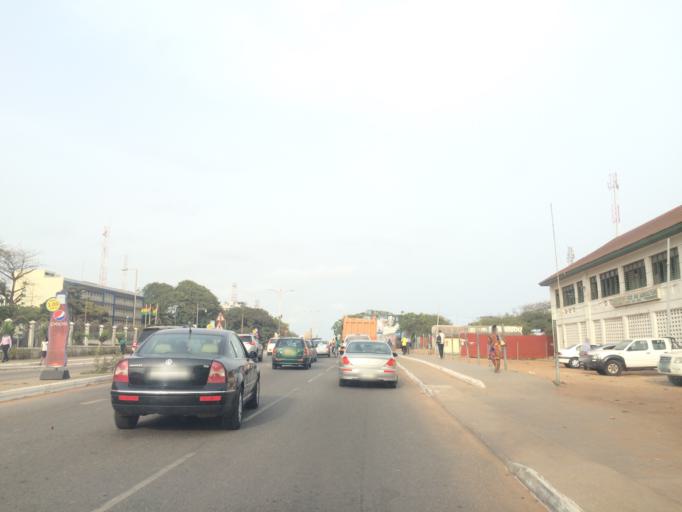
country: GH
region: Greater Accra
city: Accra
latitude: 5.5476
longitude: -0.1986
